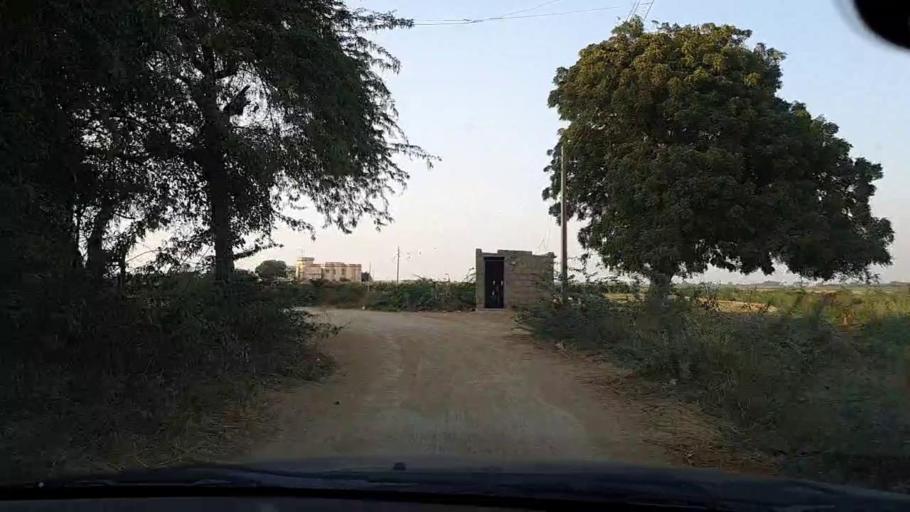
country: PK
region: Sindh
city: Thatta
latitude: 24.5622
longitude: 67.8802
